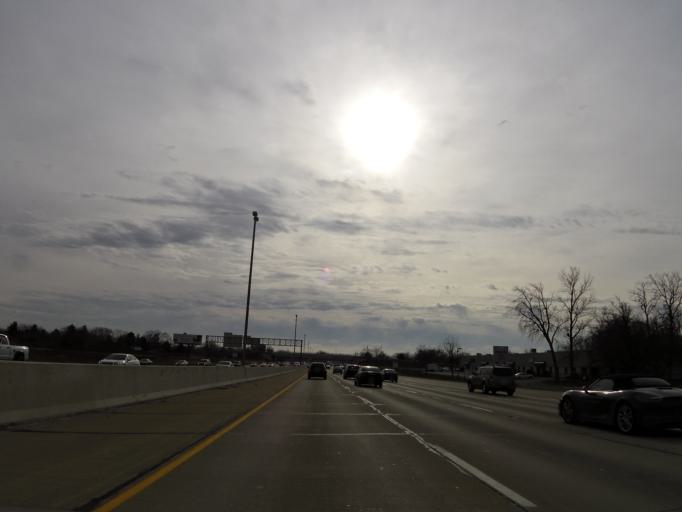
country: US
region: Indiana
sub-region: Marion County
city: Lawrence
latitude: 39.8296
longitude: -86.0342
